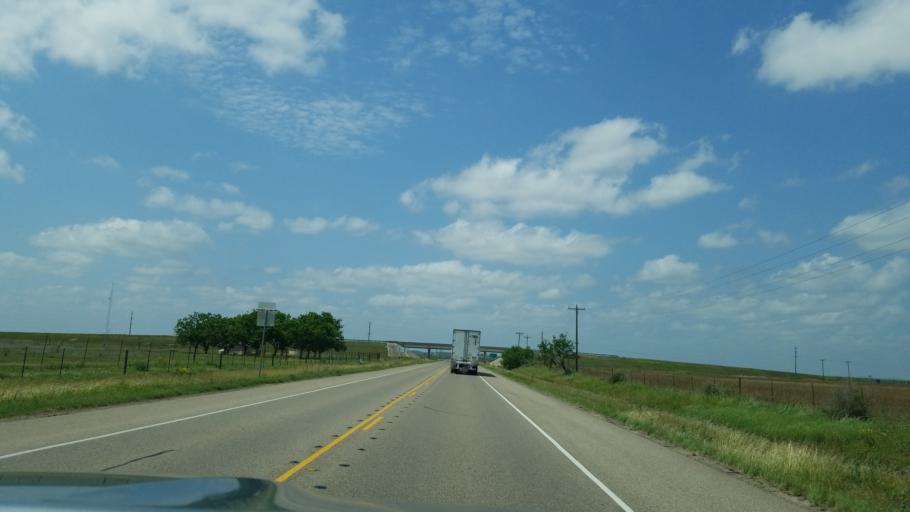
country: US
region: Texas
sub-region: Frio County
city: Pearsall
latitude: 28.9747
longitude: -99.2402
